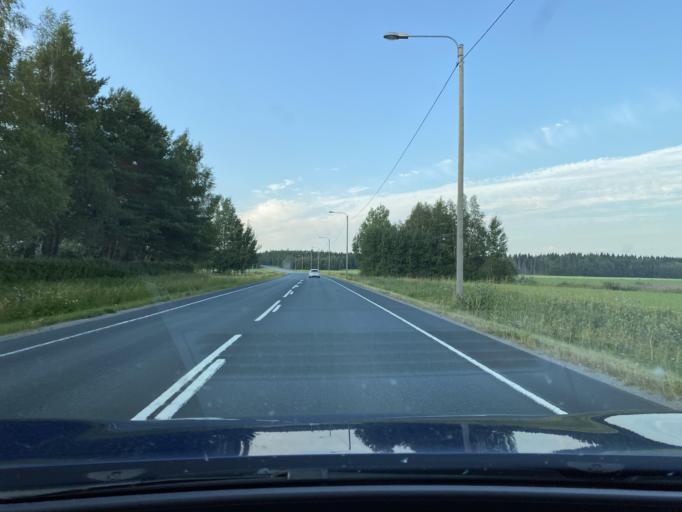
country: FI
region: Ostrobothnia
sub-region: Jakobstadsregionen
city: Bennaes
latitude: 63.6381
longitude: 22.8748
